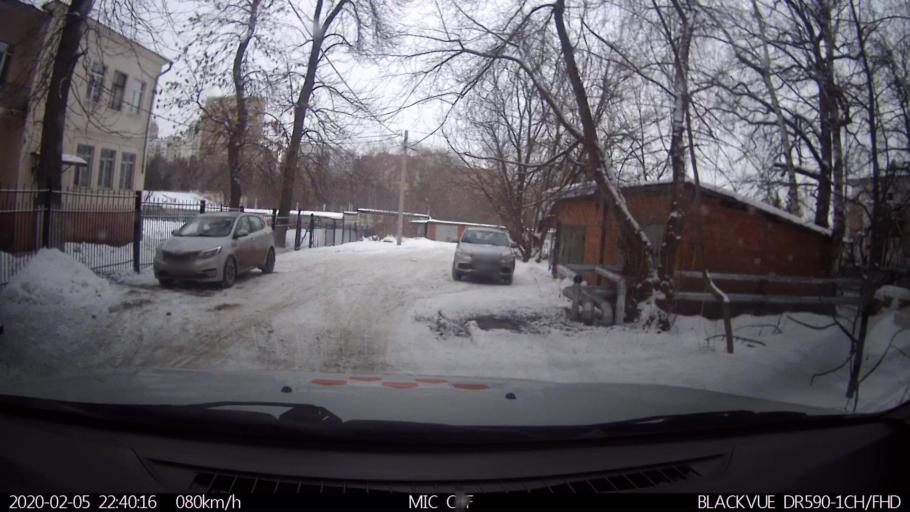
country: RU
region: Nizjnij Novgorod
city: Imeni Stepana Razina
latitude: 54.7254
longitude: 44.3104
